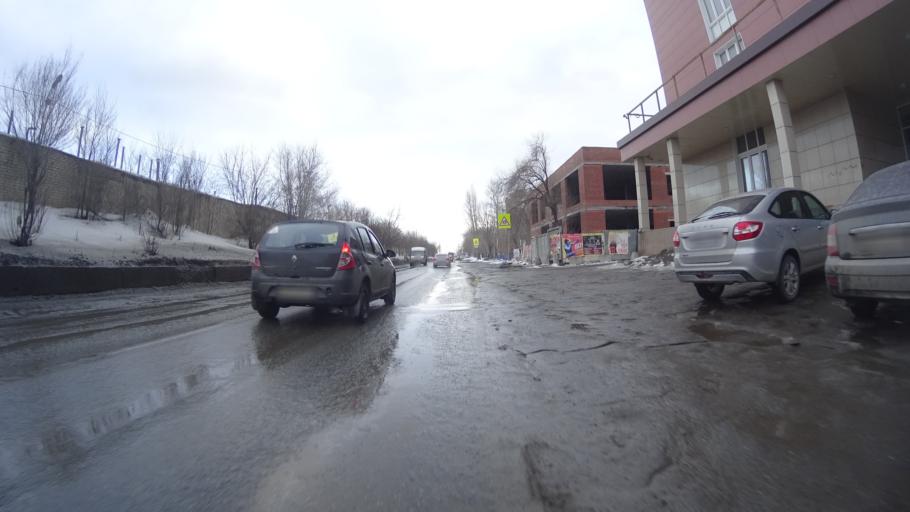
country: RU
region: Chelyabinsk
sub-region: Gorod Chelyabinsk
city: Chelyabinsk
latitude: 55.1423
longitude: 61.4011
